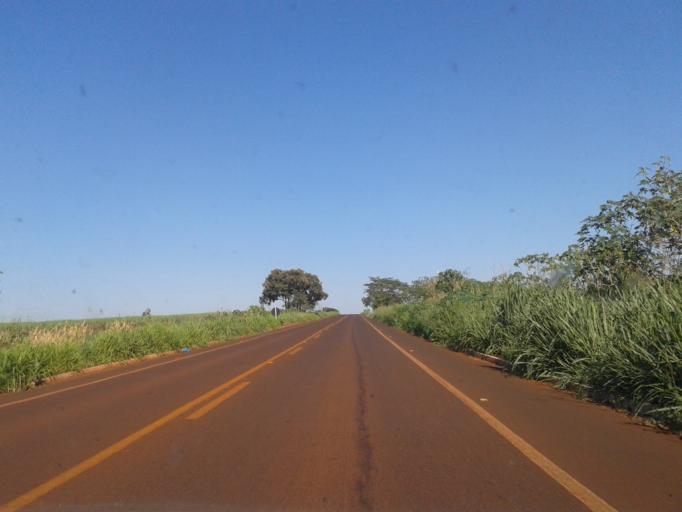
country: BR
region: Minas Gerais
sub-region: Capinopolis
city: Capinopolis
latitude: -18.7034
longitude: -49.6741
